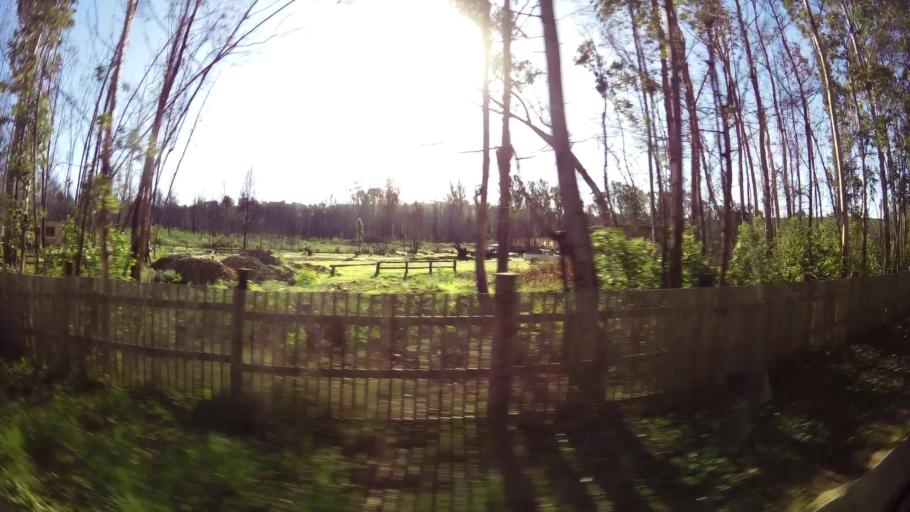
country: ZA
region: Western Cape
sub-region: Eden District Municipality
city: Knysna
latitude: -34.0292
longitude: 23.0102
